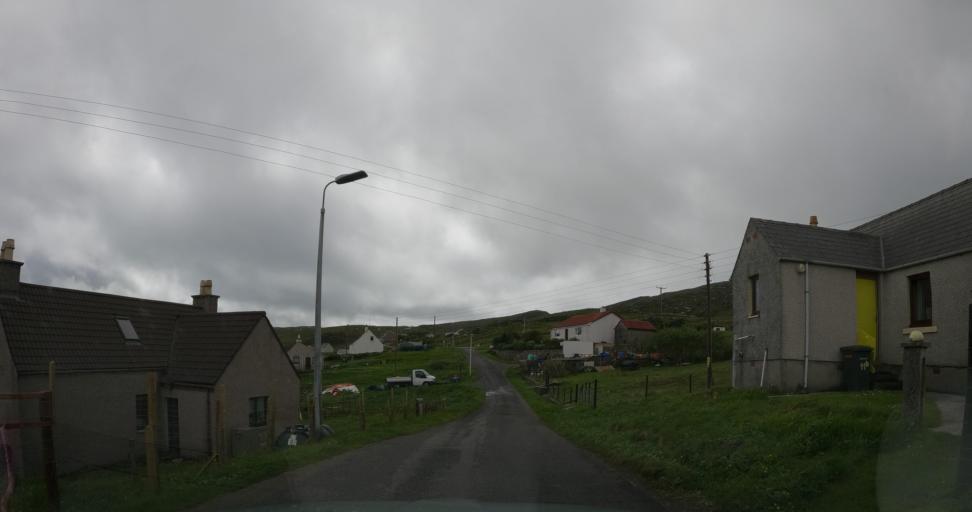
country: GB
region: Scotland
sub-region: Eilean Siar
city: Barra
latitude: 56.9569
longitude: -7.5057
